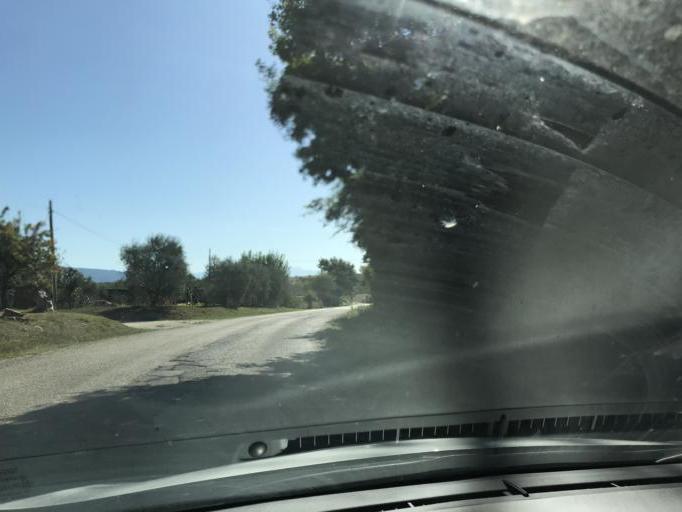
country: IT
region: Umbria
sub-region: Provincia di Terni
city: Avigliano Umbro
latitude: 42.6186
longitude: 12.4195
